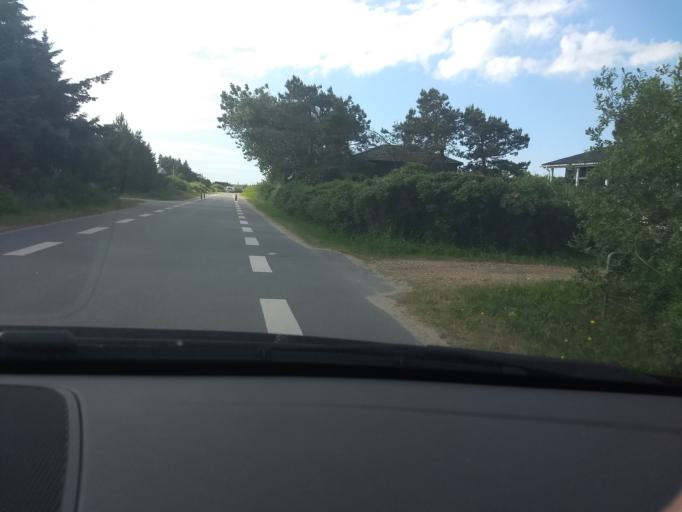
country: DE
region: Schleswig-Holstein
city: List
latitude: 55.1427
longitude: 8.4944
